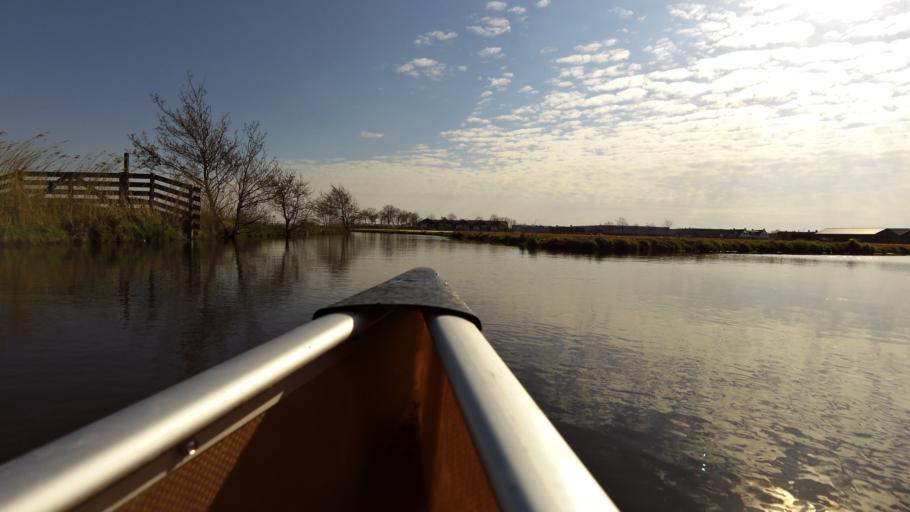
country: NL
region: South Holland
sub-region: Gemeente Lisse
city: Lisse
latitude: 52.2449
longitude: 4.5468
